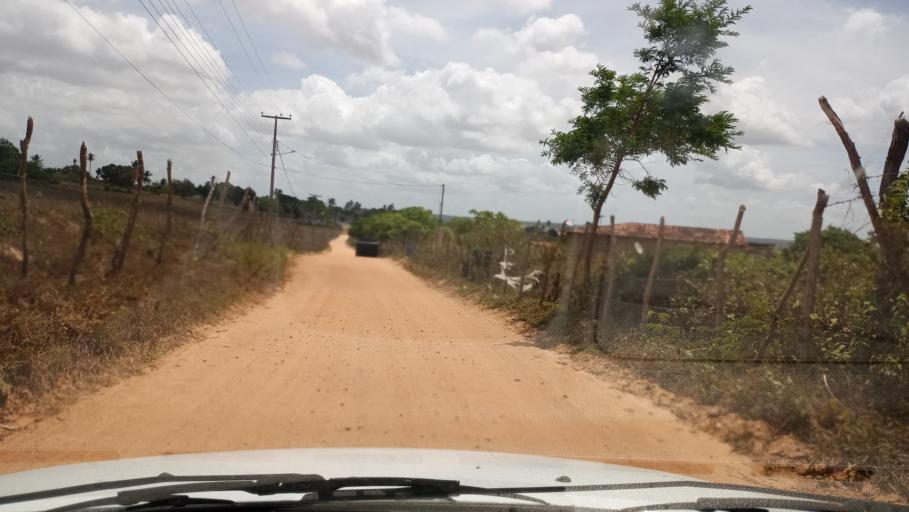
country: BR
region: Rio Grande do Norte
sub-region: Goianinha
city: Goianinha
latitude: -6.2886
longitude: -35.2850
